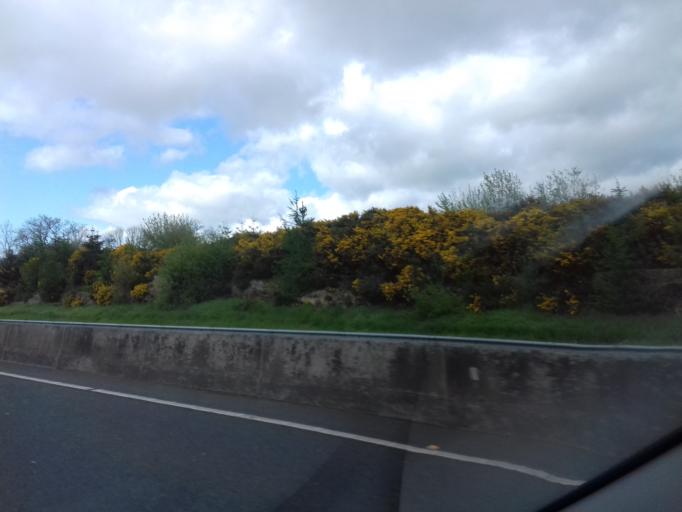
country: IE
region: Leinster
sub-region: Kilkenny
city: Thomastown
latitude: 52.4570
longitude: -7.2371
